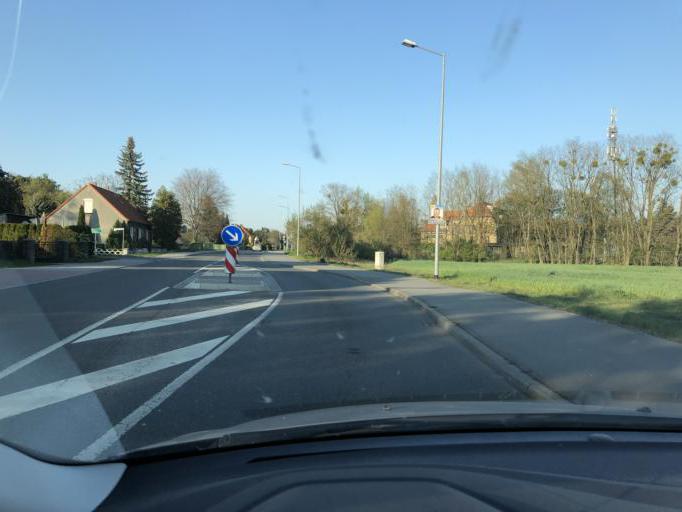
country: DE
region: Brandenburg
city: Ruhland
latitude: 51.4714
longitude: 13.8923
